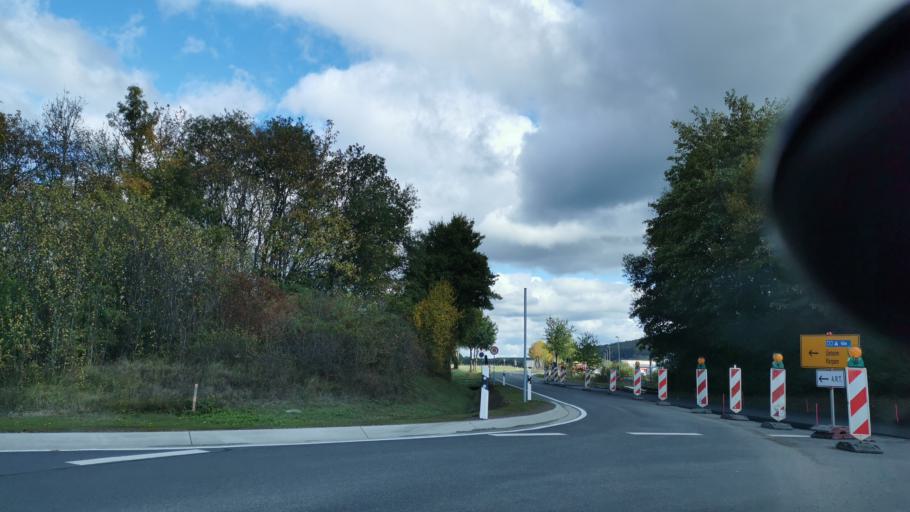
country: DE
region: Rheinland-Pfalz
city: Walsdorf
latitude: 50.2830
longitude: 6.7016
